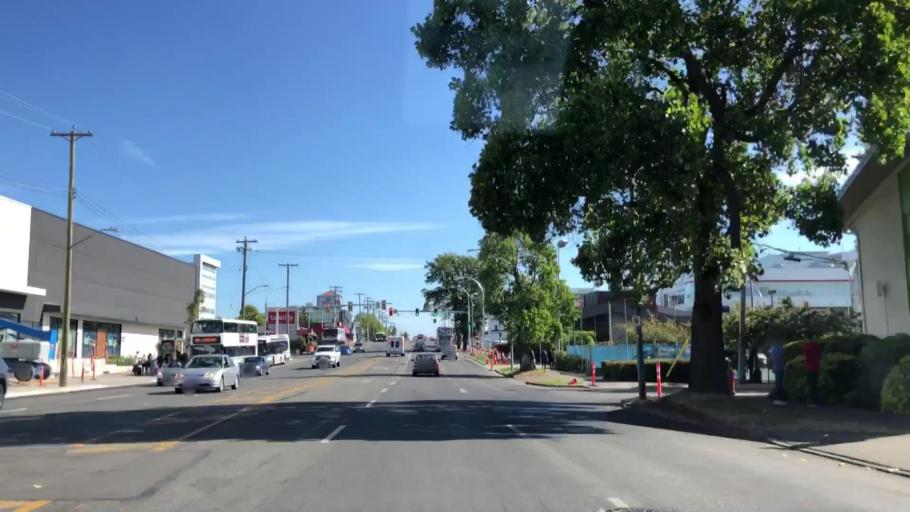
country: CA
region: British Columbia
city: Victoria
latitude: 48.4461
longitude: -123.3714
